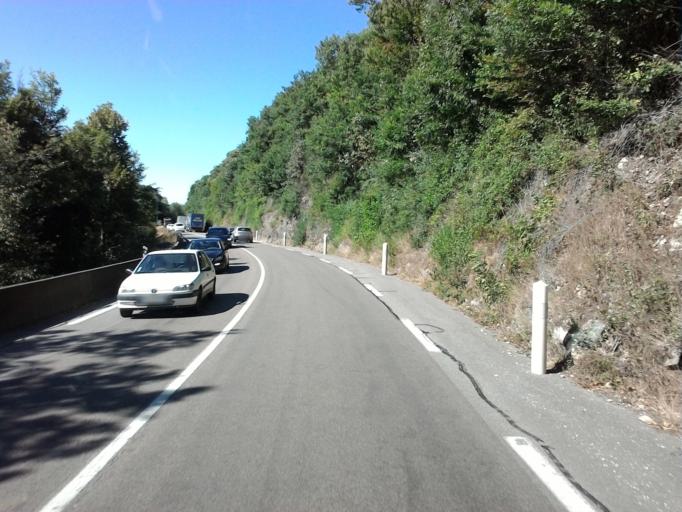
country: FR
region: Franche-Comte
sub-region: Departement du Doubs
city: Avanne-Aveney
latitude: 47.1906
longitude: 5.9664
